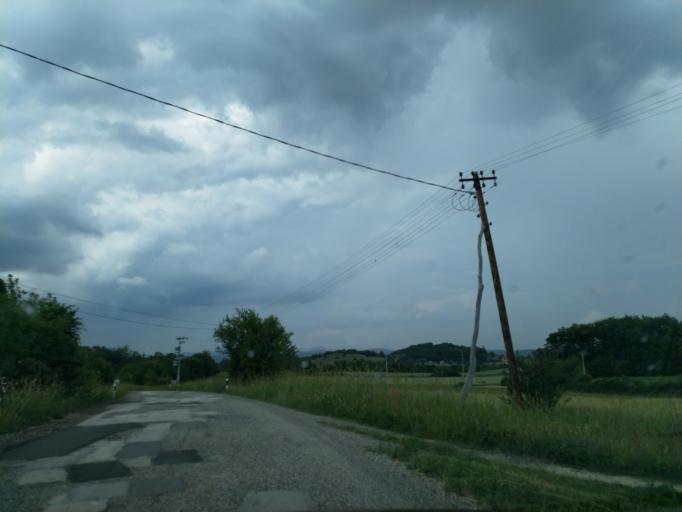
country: RS
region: Central Serbia
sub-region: Zajecarski Okrug
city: Boljevac
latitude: 43.9748
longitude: 21.9720
